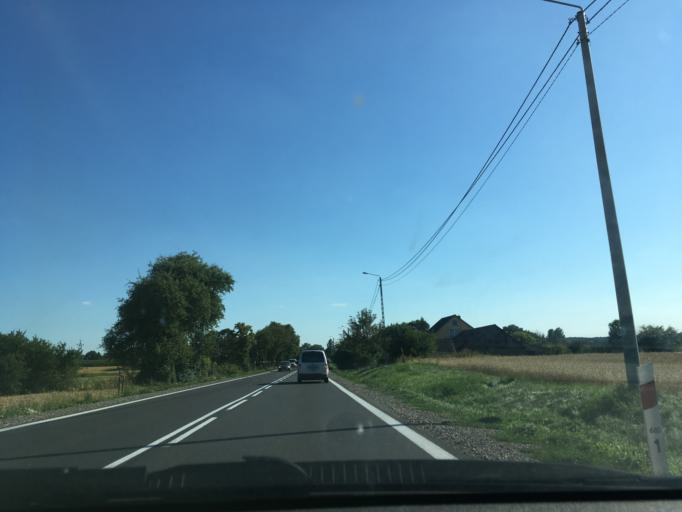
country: PL
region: Podlasie
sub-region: Powiat sokolski
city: Suchowola
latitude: 53.4697
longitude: 23.0901
